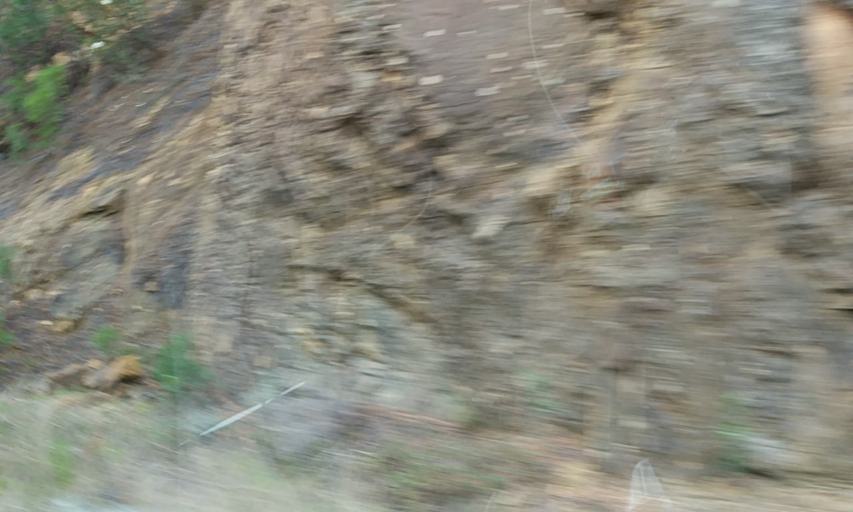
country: ES
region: Extremadura
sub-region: Provincia de Caceres
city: Acebo
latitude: 40.2033
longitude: -6.6762
